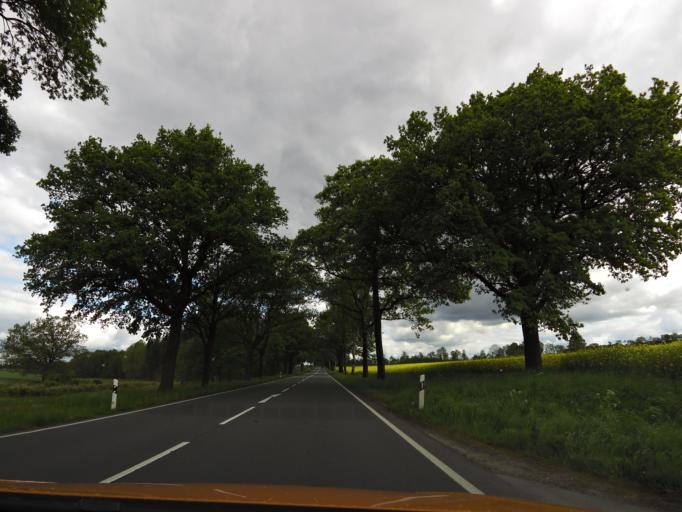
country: DE
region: Lower Saxony
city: Bassum
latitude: 52.8790
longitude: 8.7286
